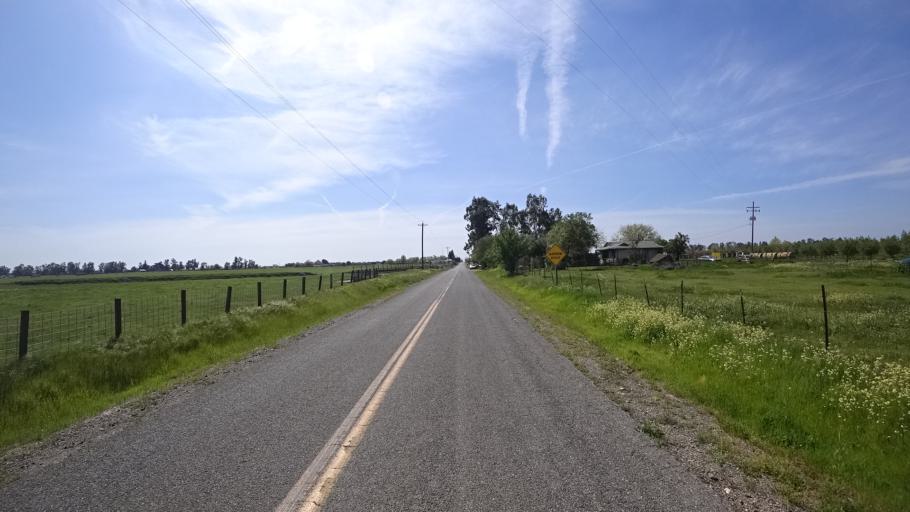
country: US
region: California
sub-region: Glenn County
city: Hamilton City
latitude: 39.8037
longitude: -122.0852
